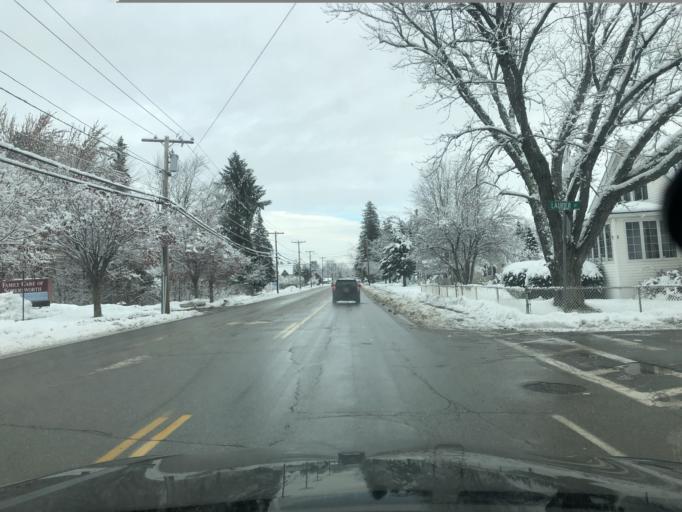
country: US
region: New Hampshire
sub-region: Strafford County
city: Somersworth
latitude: 43.2445
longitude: -70.8761
